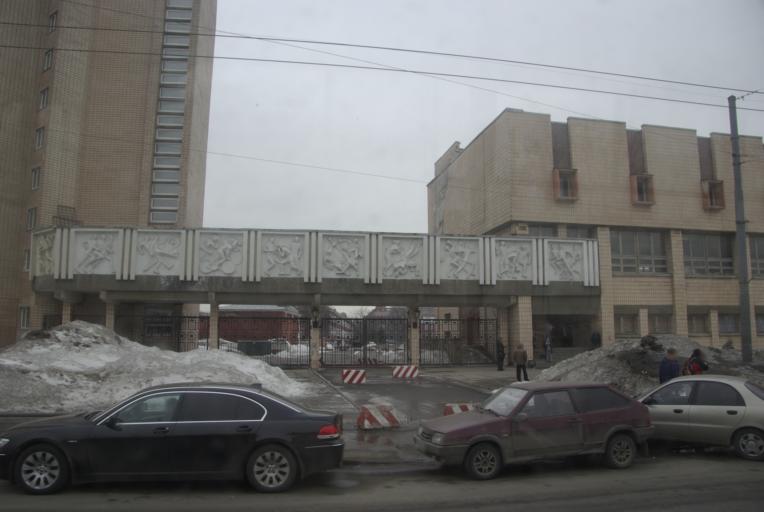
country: RU
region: Leningrad
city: Sampsonievskiy
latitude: 59.9756
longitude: 30.3453
